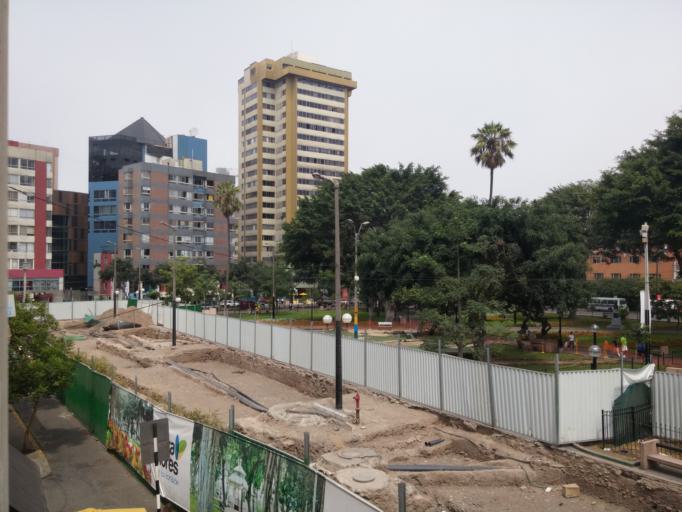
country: PE
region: Lima
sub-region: Lima
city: San Isidro
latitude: -12.1220
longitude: -77.0301
